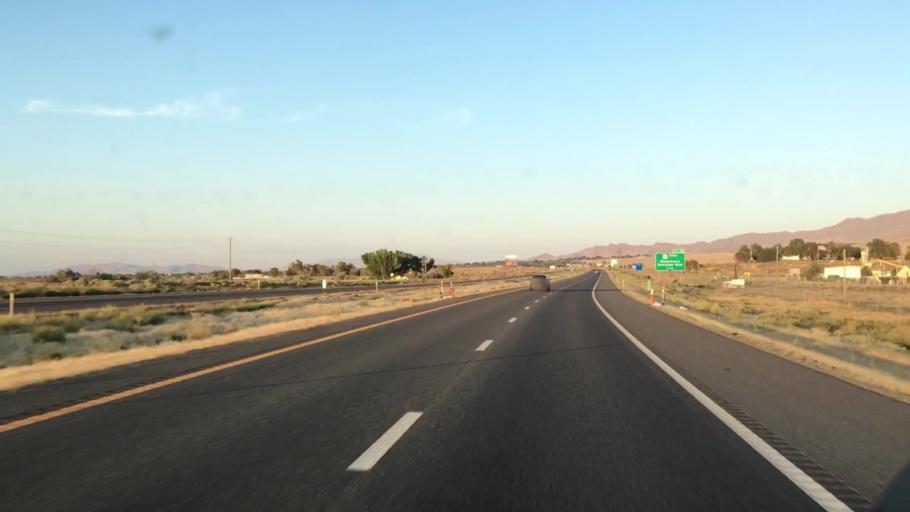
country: US
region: Nevada
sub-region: Humboldt County
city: Winnemucca
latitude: 40.9429
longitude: -117.7764
